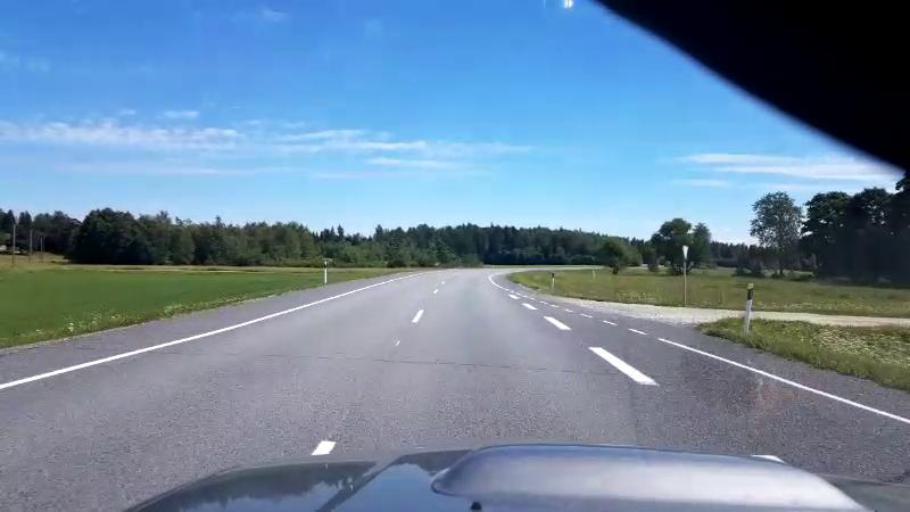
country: EE
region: Jaervamaa
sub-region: Jaerva-Jaani vald
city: Jarva-Jaani
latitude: 59.0013
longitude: 25.9356
